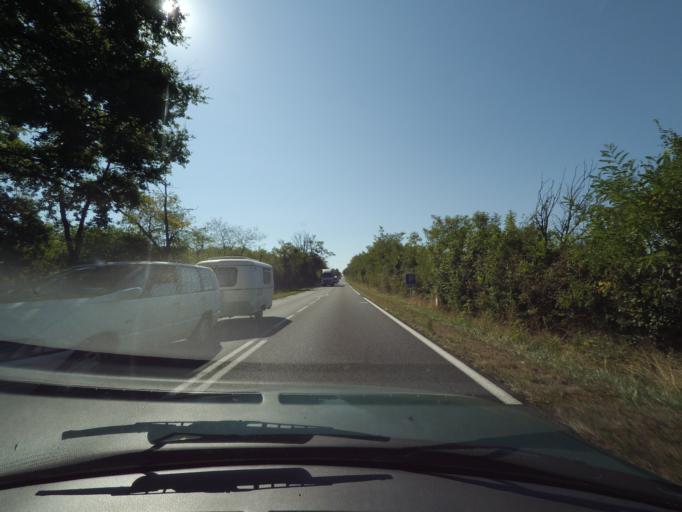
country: FR
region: Poitou-Charentes
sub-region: Departement de la Vienne
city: Lussac-les-Chateaux
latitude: 46.3476
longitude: 0.7914
